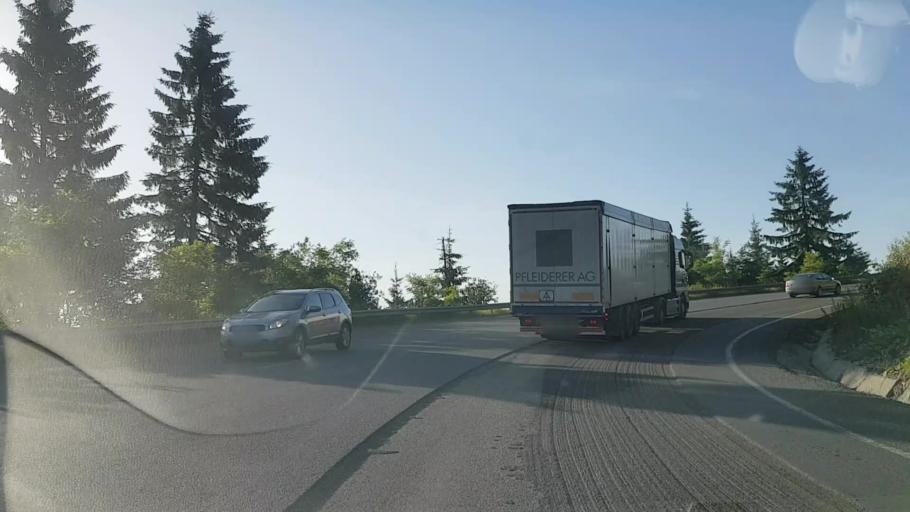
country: RO
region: Bistrita-Nasaud
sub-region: Comuna Lunca Ilvei
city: Lunca Ilvei
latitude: 47.2643
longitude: 25.0199
